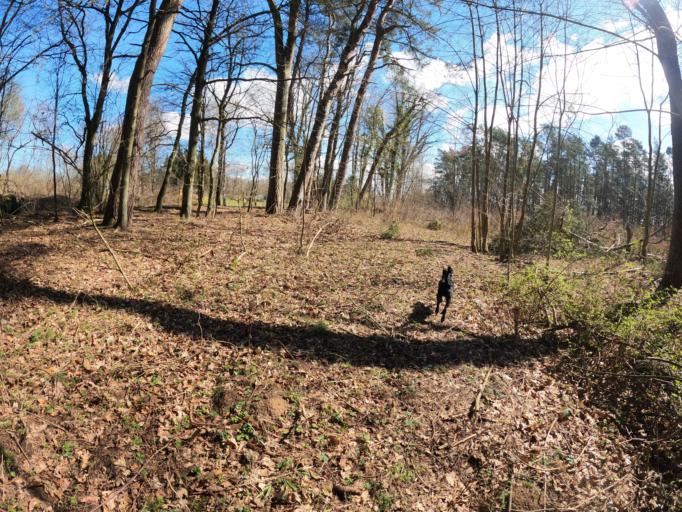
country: PL
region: West Pomeranian Voivodeship
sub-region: Powiat gryficki
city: Gryfice
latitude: 53.9245
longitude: 15.2293
